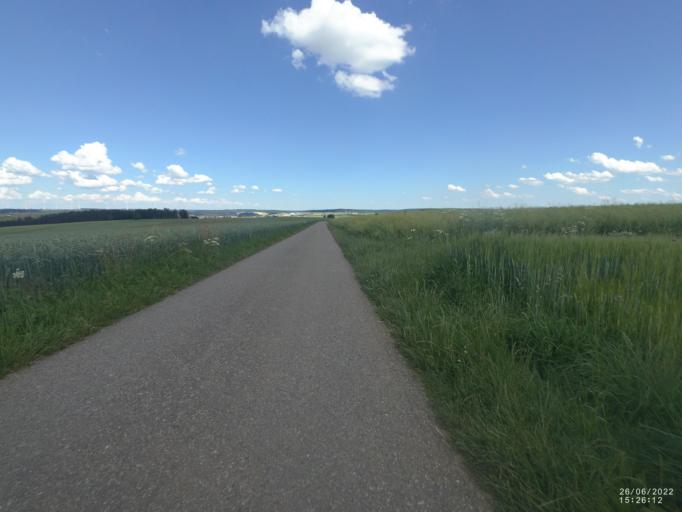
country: DE
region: Baden-Wuerttemberg
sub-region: Regierungsbezirk Stuttgart
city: Bohmenkirch
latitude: 48.6578
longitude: 9.9497
